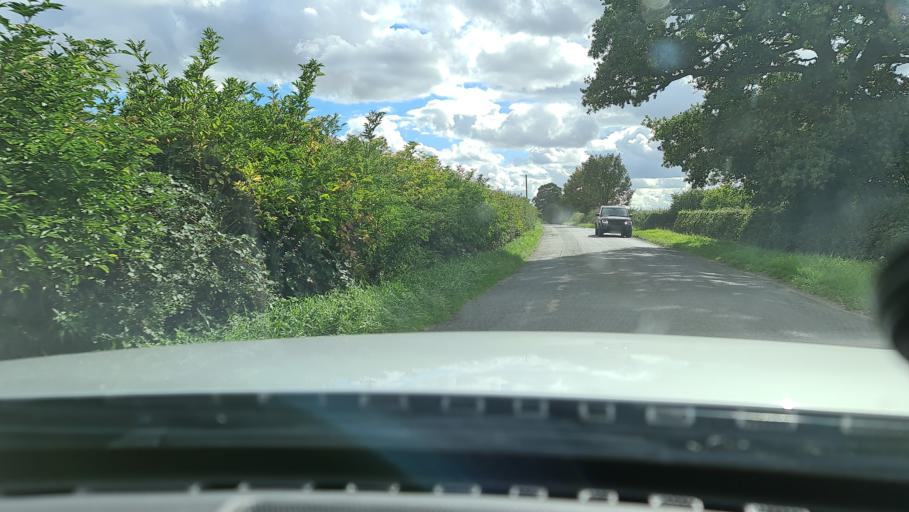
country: GB
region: England
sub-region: Oxfordshire
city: Somerton
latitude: 51.9745
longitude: -1.2360
